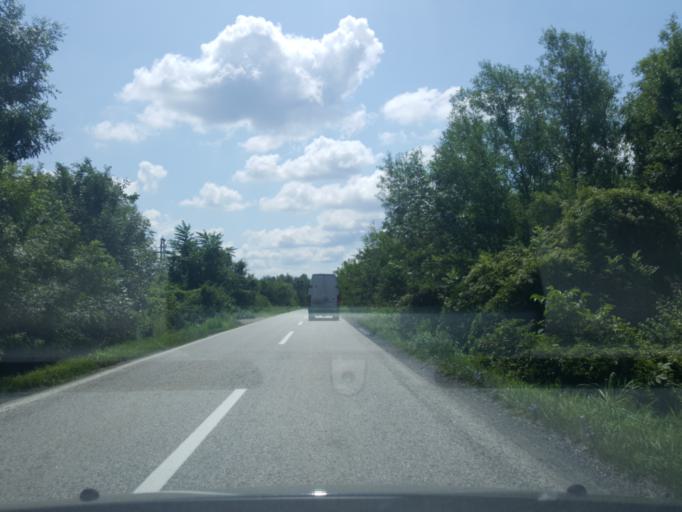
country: RS
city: Glusci
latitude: 44.9087
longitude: 19.5456
